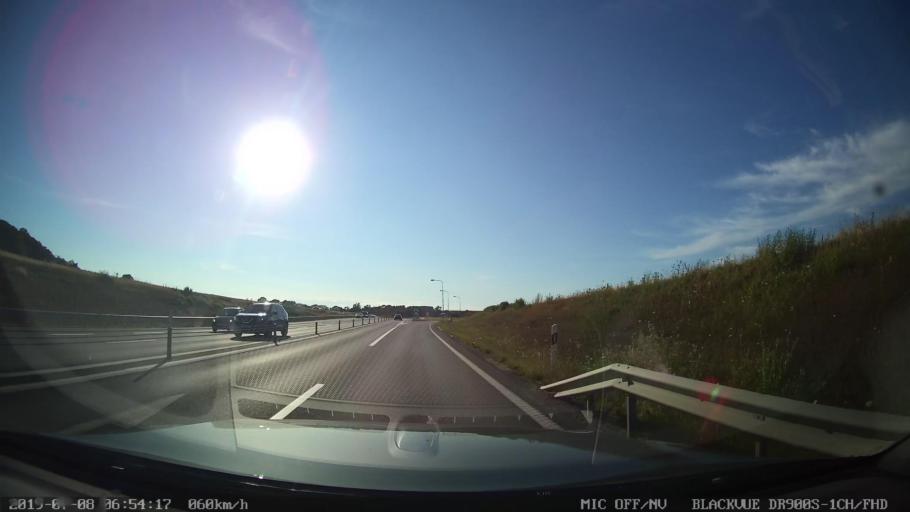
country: SE
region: Skane
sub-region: Helsingborg
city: Odakra
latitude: 56.0824
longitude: 12.7177
